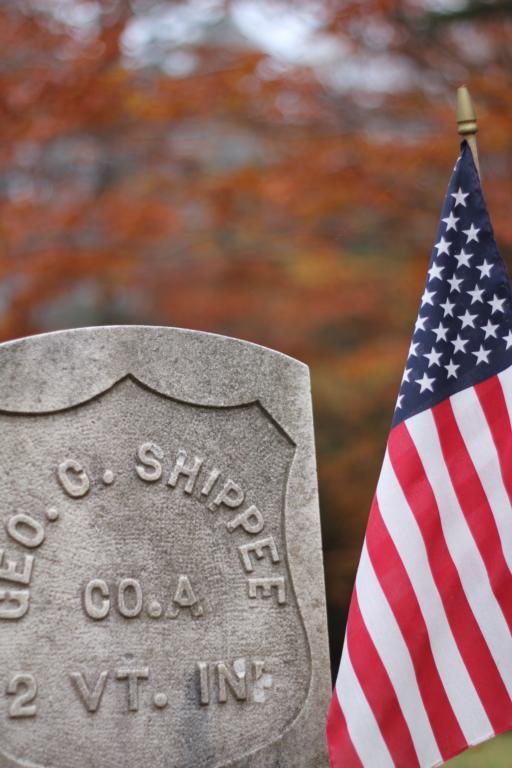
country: US
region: Vermont
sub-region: Windham County
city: Dover
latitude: 42.8947
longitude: -72.9758
